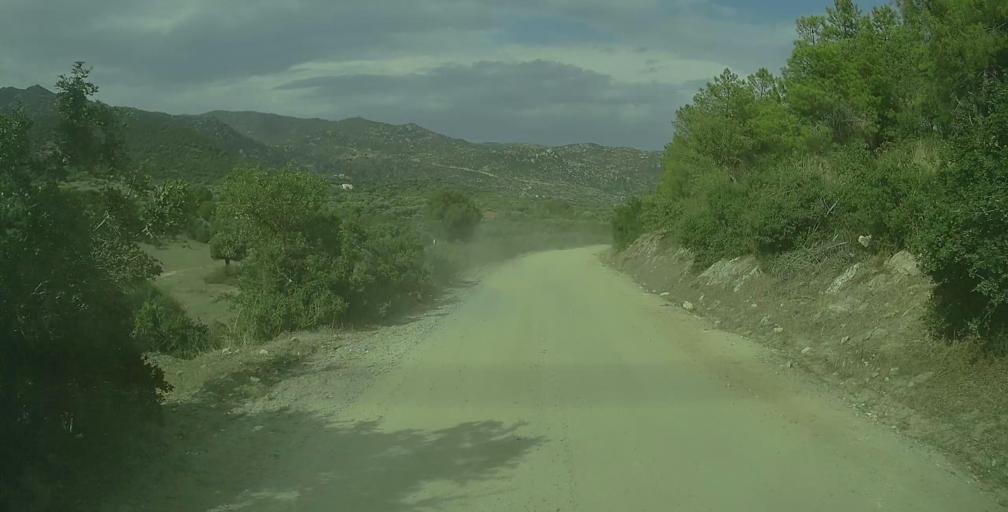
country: GR
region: Central Macedonia
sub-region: Nomos Chalkidikis
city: Sykia
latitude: 40.0237
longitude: 23.9453
